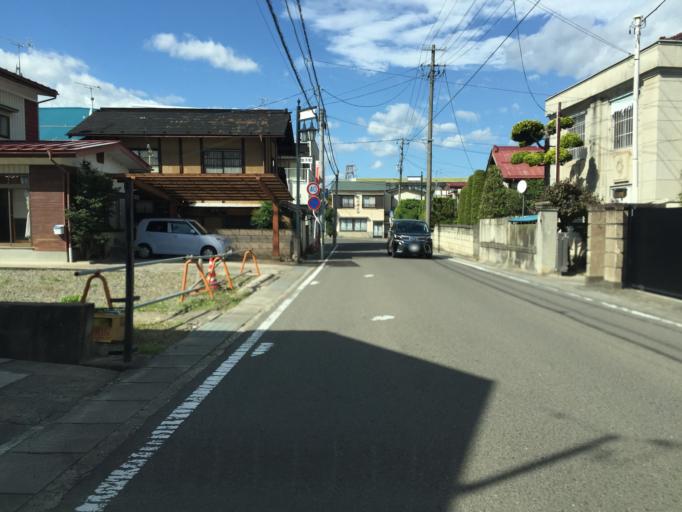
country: JP
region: Fukushima
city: Hobaramachi
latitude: 37.7798
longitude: 140.5960
